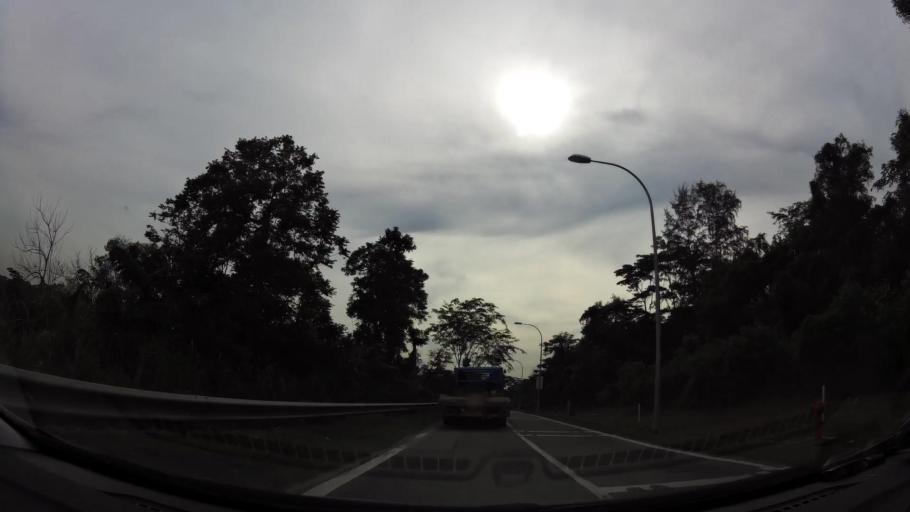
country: MY
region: Johor
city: Johor Bahru
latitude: 1.4239
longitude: 103.7204
